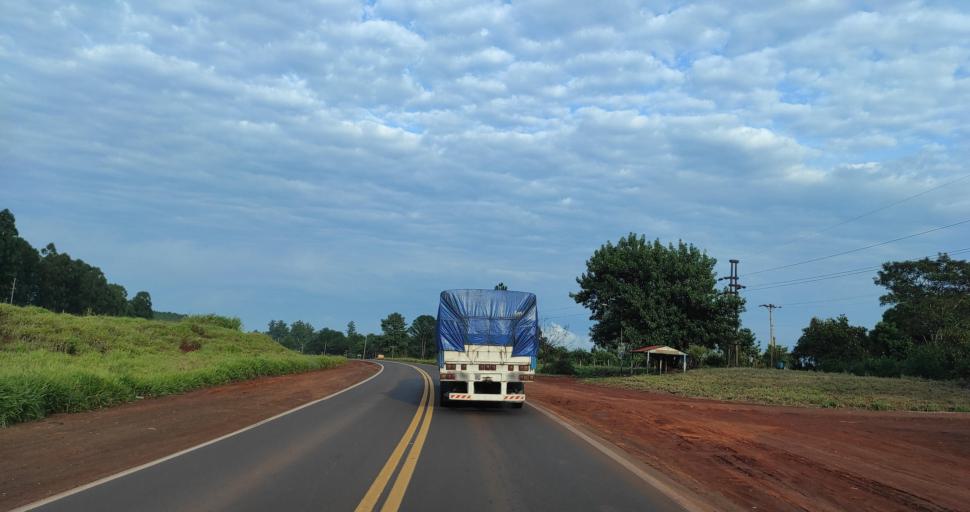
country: AR
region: Corrientes
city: Gobernador Ingeniero Valentin Virasoro
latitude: -27.9397
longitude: -55.9808
